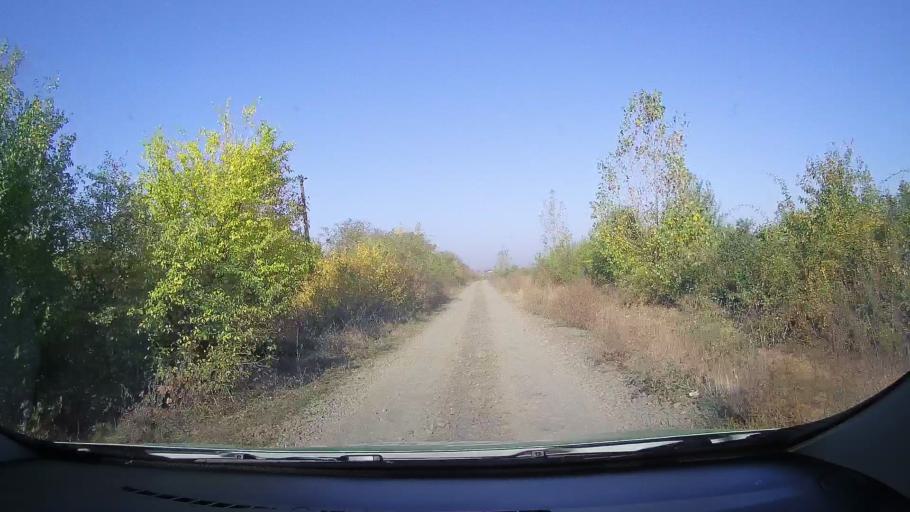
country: RO
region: Satu Mare
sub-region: Comuna Sauca
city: Sauca
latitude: 47.4759
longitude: 22.4776
